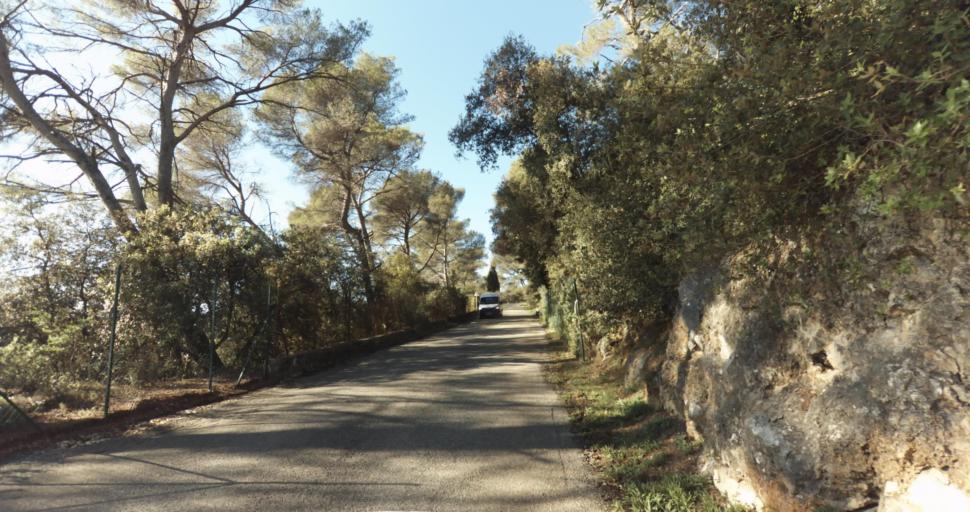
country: FR
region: Provence-Alpes-Cote d'Azur
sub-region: Departement des Alpes-Maritimes
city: Vence
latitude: 43.7136
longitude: 7.1163
